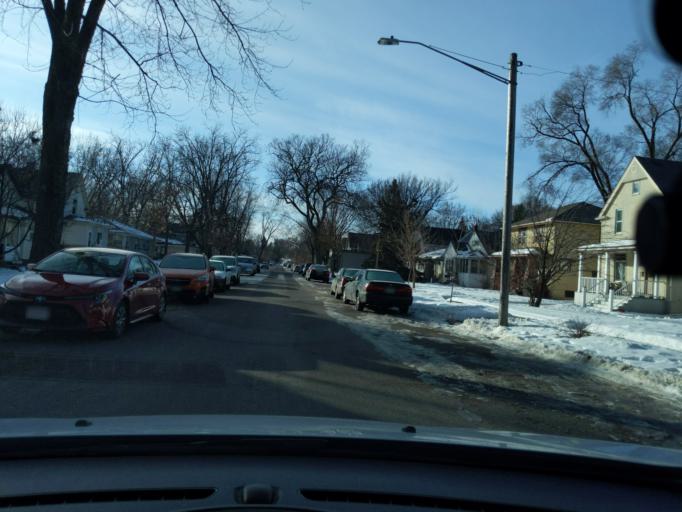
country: US
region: Minnesota
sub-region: Ramsey County
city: Lauderdale
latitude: 44.9906
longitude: -93.2177
